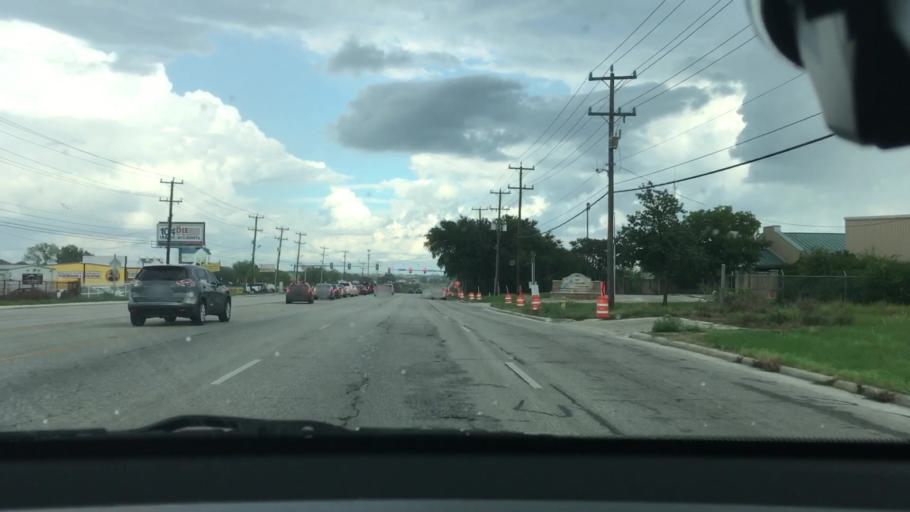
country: US
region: Texas
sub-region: Bexar County
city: Windcrest
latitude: 29.5020
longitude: -98.3615
